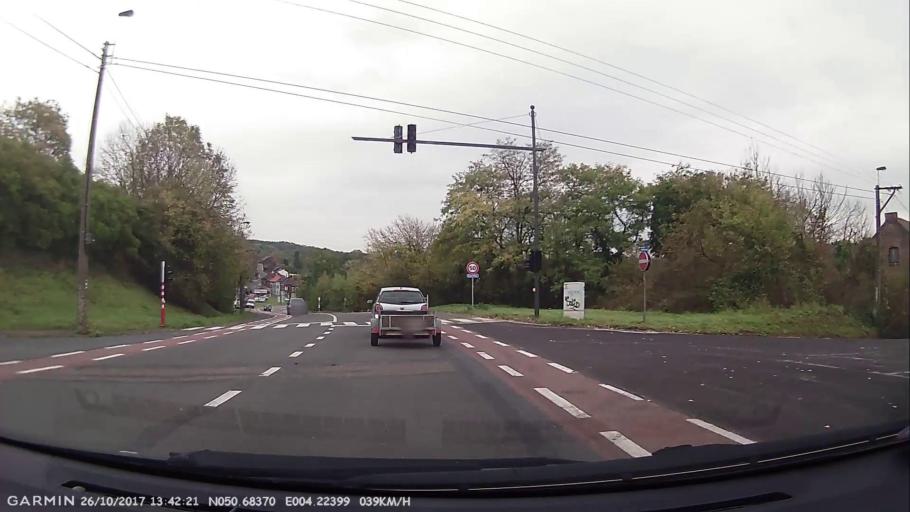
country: BE
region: Wallonia
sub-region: Province du Brabant Wallon
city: Tubize
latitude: 50.6835
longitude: 4.2246
